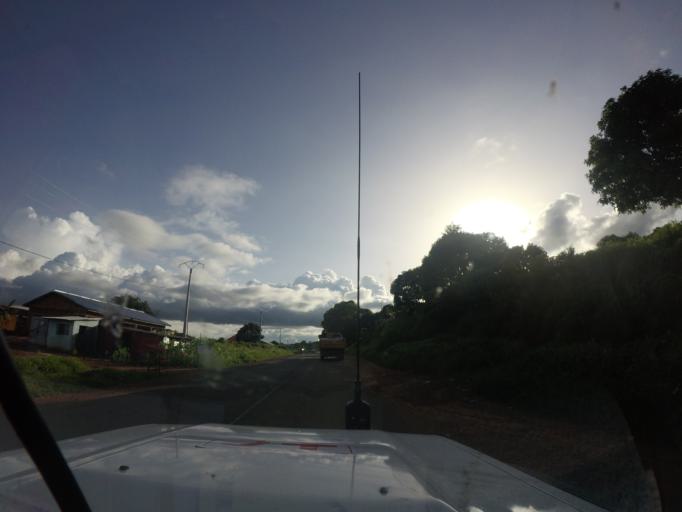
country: GN
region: Kindia
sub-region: Kindia
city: Kindia
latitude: 10.0322
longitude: -12.8658
